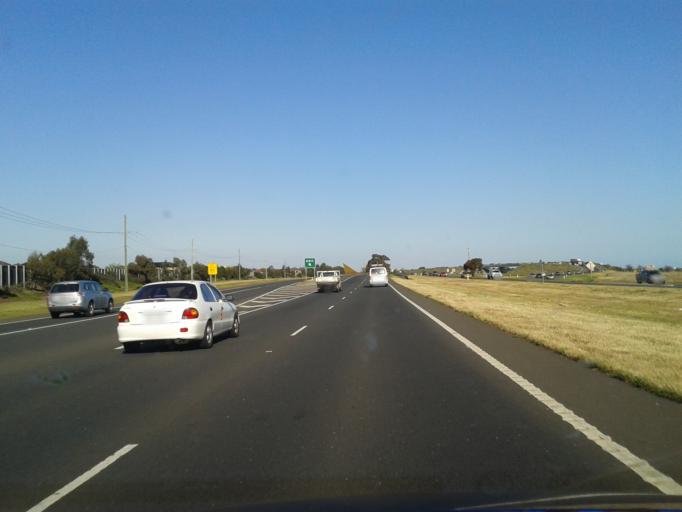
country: AU
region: Victoria
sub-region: Melton
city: Caroline Springs
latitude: -37.7519
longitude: 144.7278
